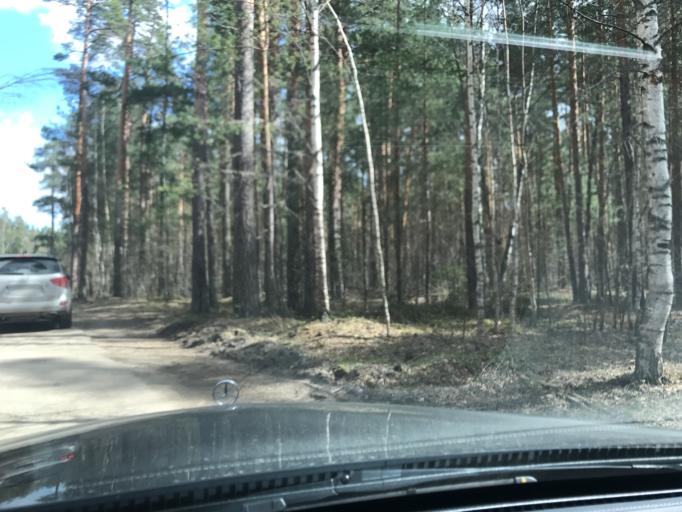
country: RU
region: Moskovskaya
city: Vereya
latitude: 55.8388
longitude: 39.1218
